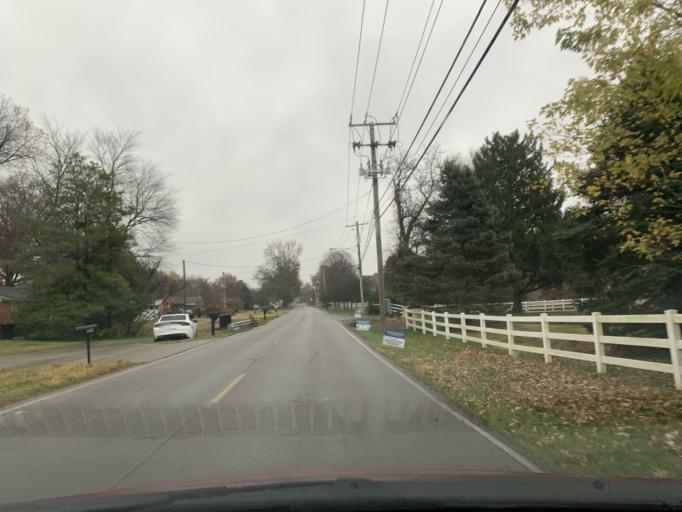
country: US
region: Kentucky
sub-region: Jefferson County
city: Buechel
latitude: 38.1981
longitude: -85.6369
